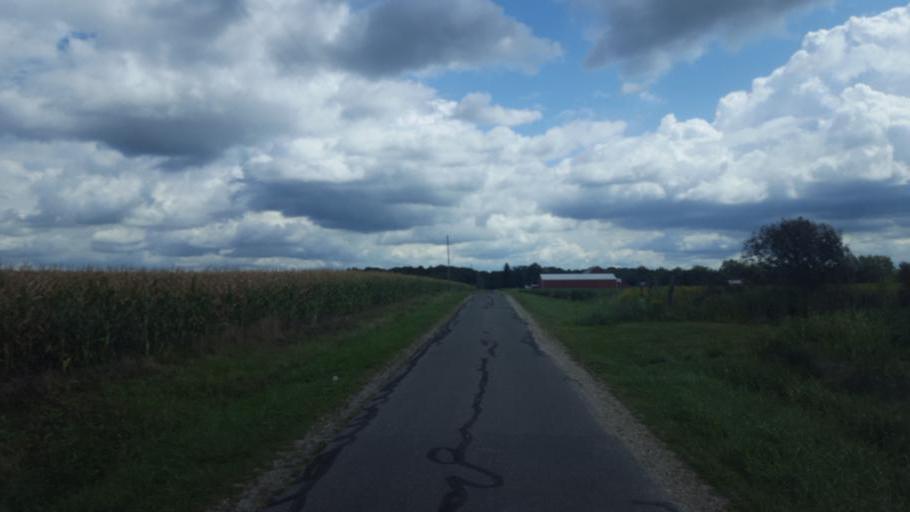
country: US
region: Ohio
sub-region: Huron County
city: Willard
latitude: 41.1155
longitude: -82.7813
